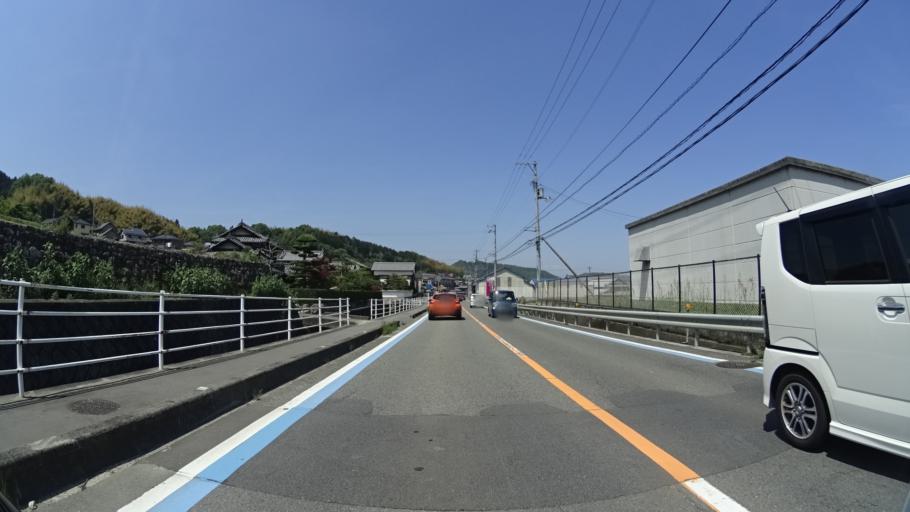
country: JP
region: Ehime
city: Hojo
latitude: 34.0105
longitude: 132.9376
